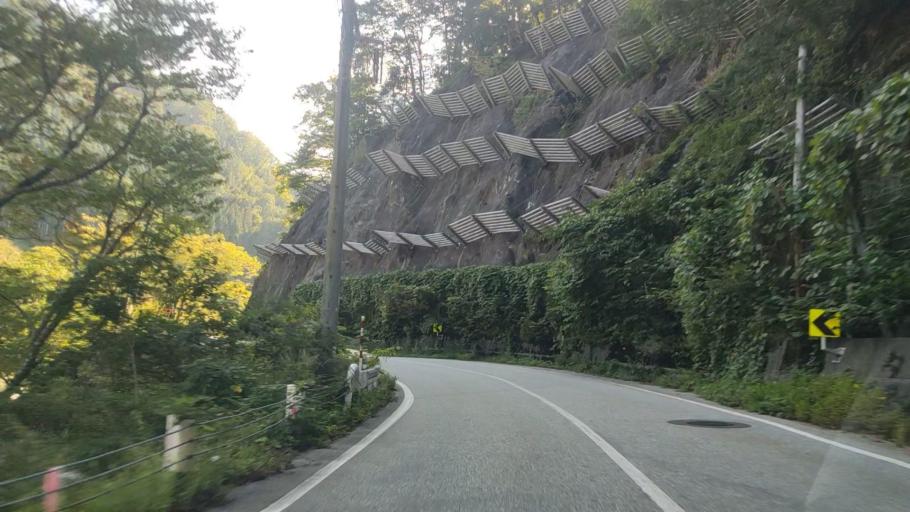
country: JP
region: Gifu
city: Takayama
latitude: 36.2978
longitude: 137.1229
